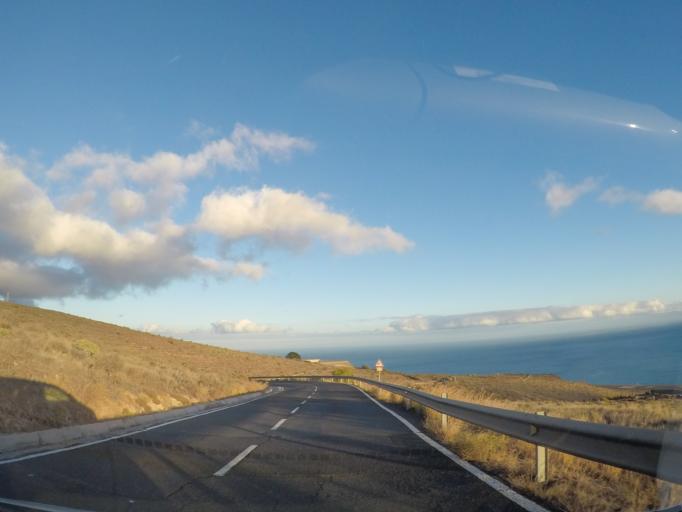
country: ES
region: Canary Islands
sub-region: Provincia de Santa Cruz de Tenerife
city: Alajero
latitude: 28.0394
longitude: -17.2285
